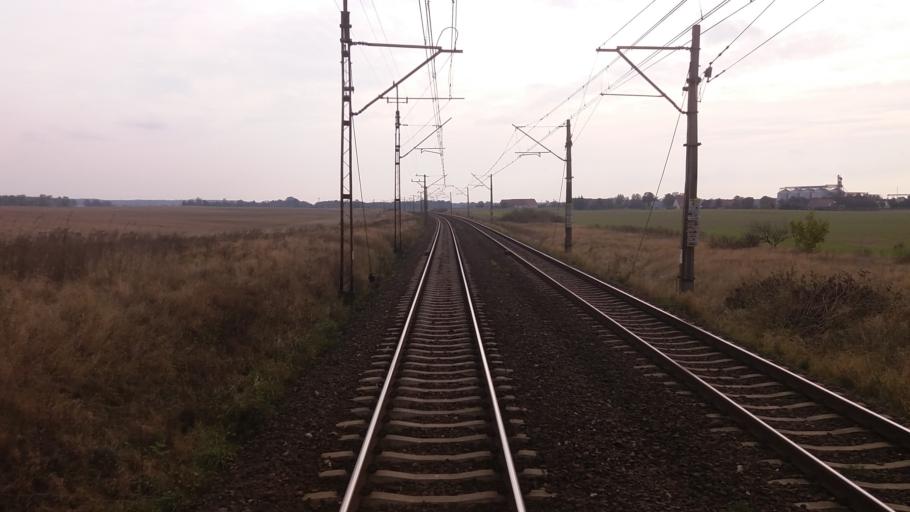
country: PL
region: West Pomeranian Voivodeship
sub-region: Powiat stargardzki
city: Dolice
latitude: 53.2343
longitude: 15.1336
